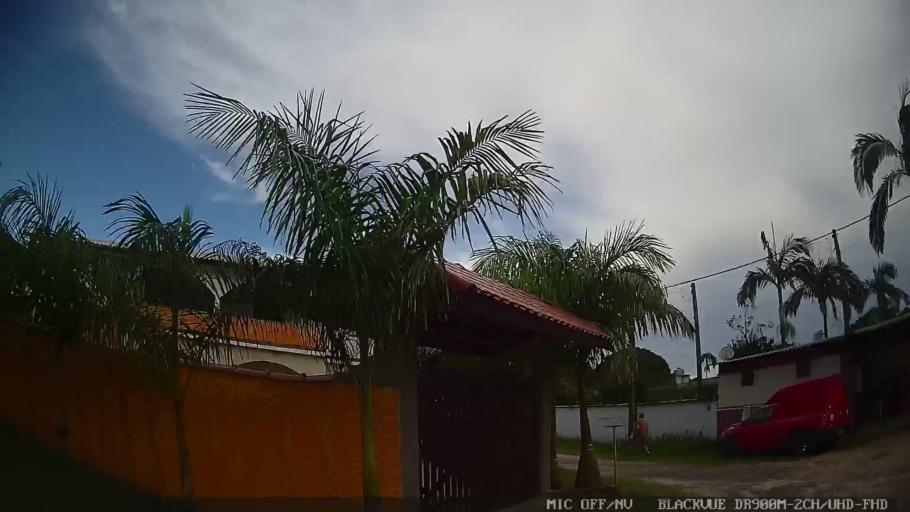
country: BR
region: Sao Paulo
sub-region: Iguape
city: Iguape
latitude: -24.6579
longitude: -47.4120
